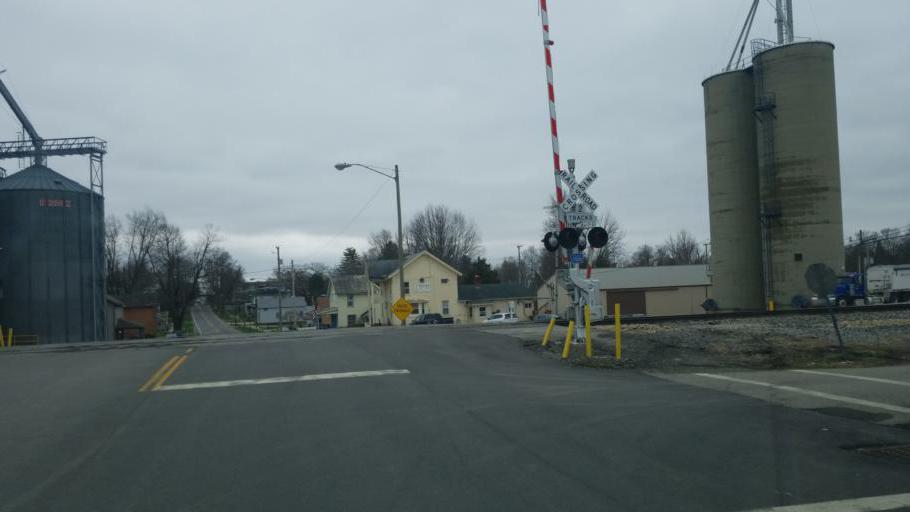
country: US
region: Ohio
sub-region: Wyandot County
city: Upper Sandusky
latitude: 40.8179
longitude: -83.1309
